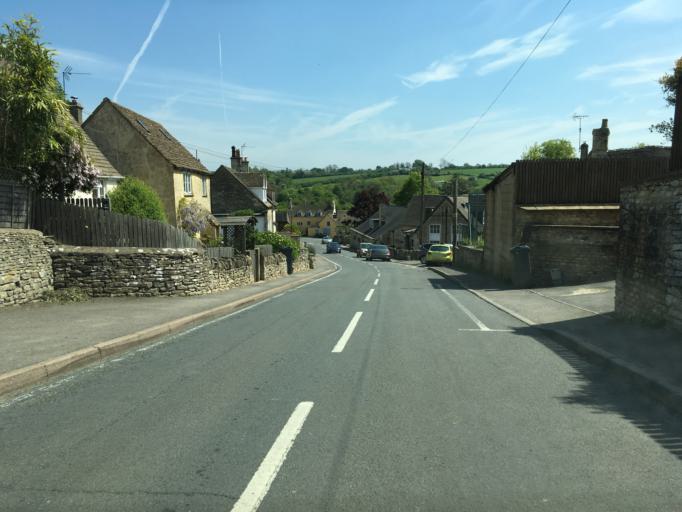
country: GB
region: England
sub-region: Gloucestershire
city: Nailsworth
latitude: 51.6816
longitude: -2.2365
